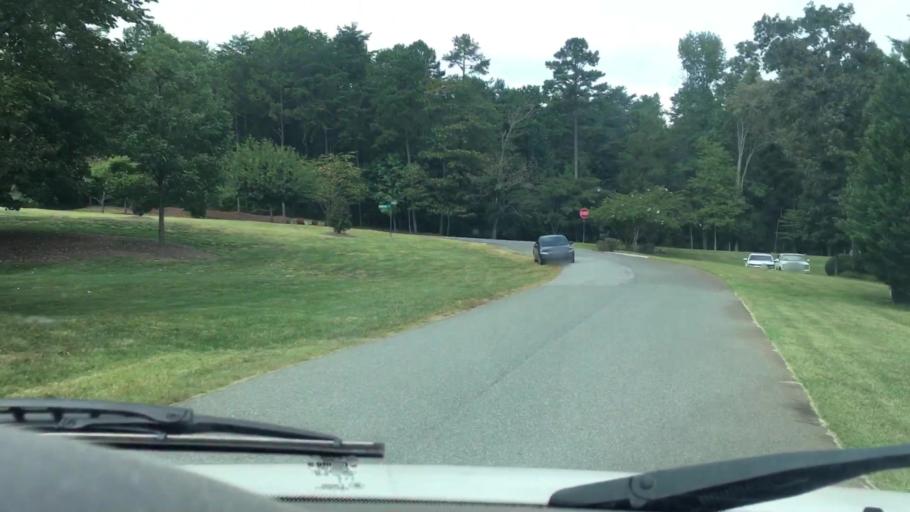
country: US
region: North Carolina
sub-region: Gaston County
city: Davidson
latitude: 35.5170
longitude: -80.7984
